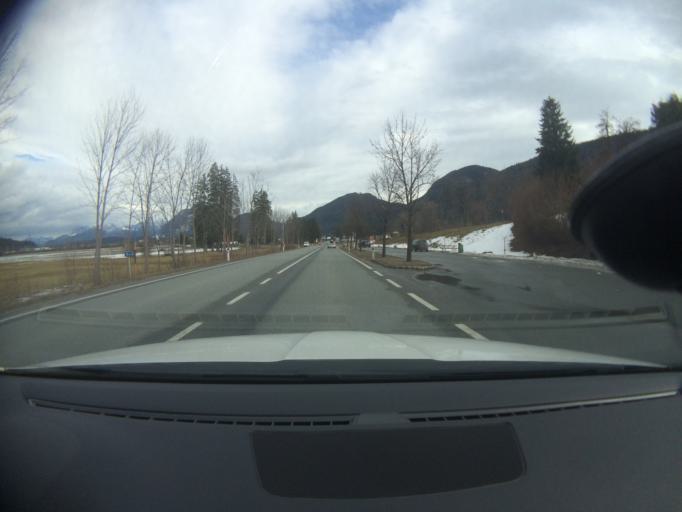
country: AT
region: Tyrol
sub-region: Politischer Bezirk Kufstein
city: Worgl
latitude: 47.4785
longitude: 12.0351
